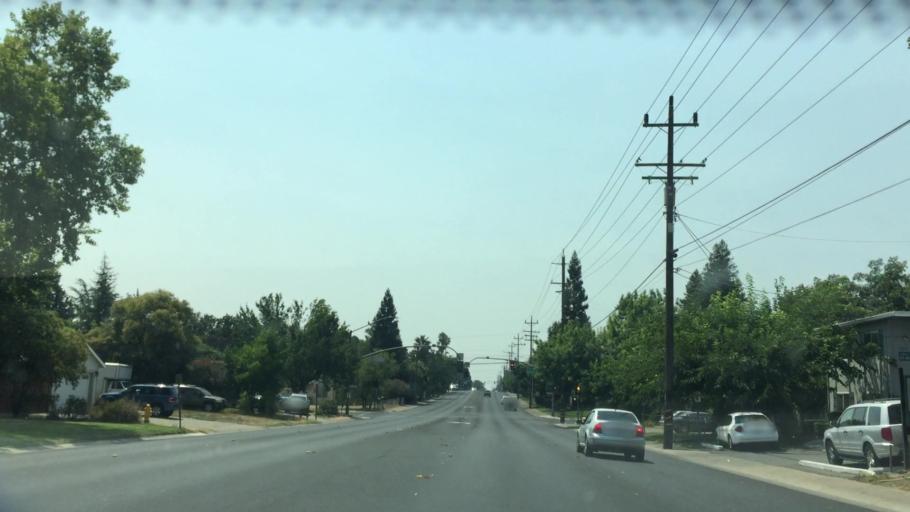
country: US
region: California
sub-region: Sacramento County
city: Arden-Arcade
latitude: 38.6221
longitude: -121.3645
